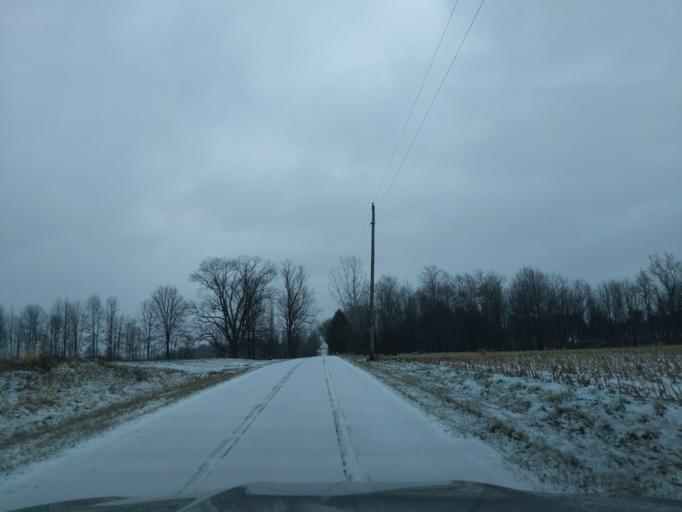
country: US
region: Indiana
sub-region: Decatur County
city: Westport
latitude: 39.2048
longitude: -85.4907
